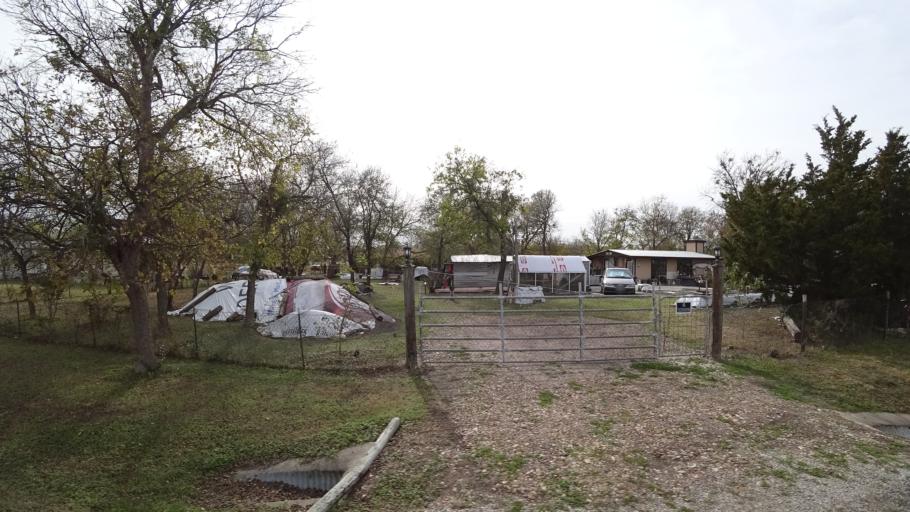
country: US
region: Texas
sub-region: Travis County
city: Garfield
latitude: 30.1304
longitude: -97.6212
